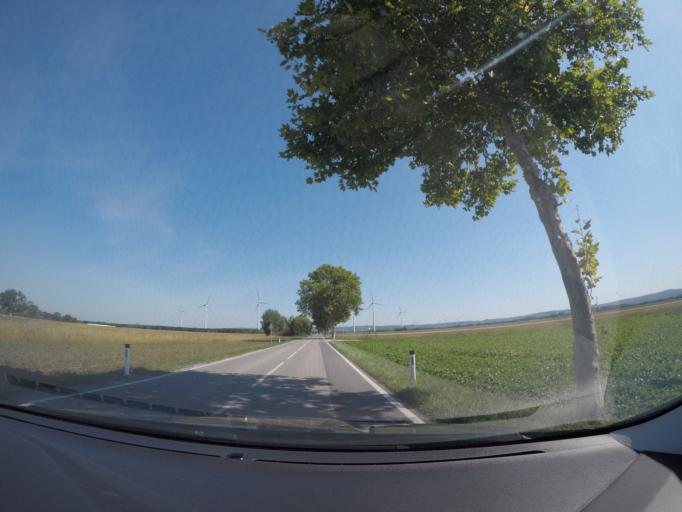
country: AT
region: Lower Austria
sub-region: Politischer Bezirk Baden
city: Mitterndorf an der Fischa
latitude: 47.9626
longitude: 16.4694
